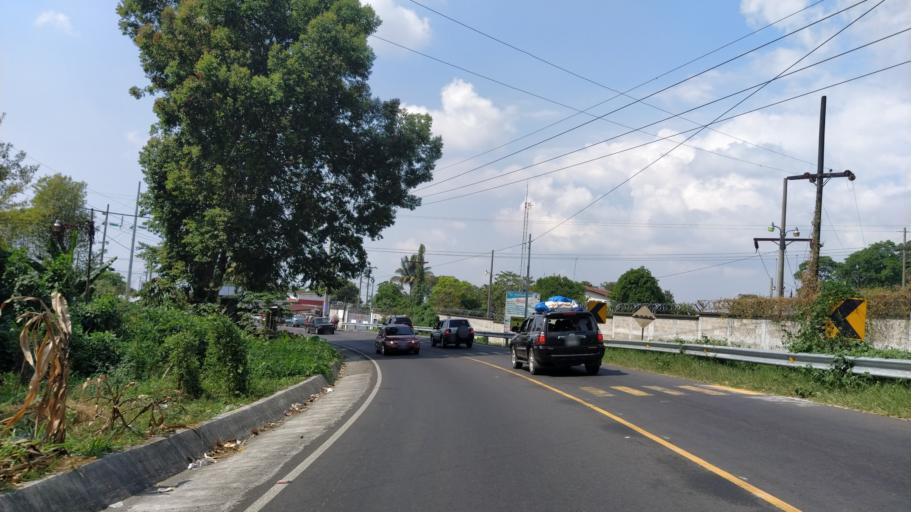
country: GT
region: Retalhuleu
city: San Felipe
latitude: 14.6209
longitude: -91.5894
